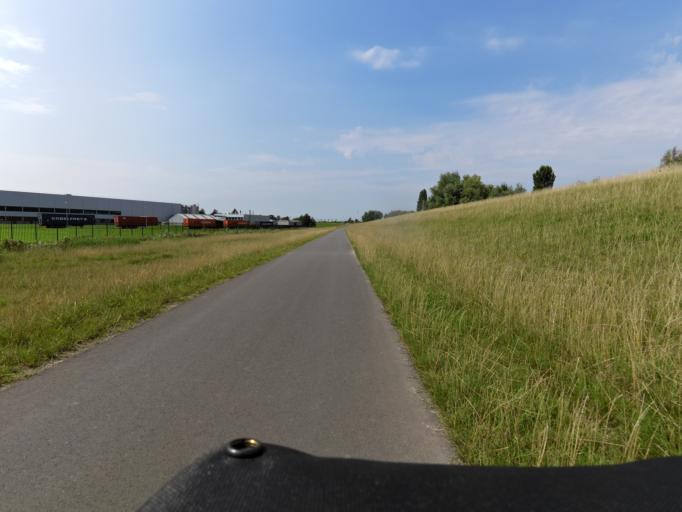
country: NL
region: South Holland
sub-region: Gemeente Oud-Beijerland
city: Oud-Beijerland
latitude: 51.8317
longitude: 4.4425
